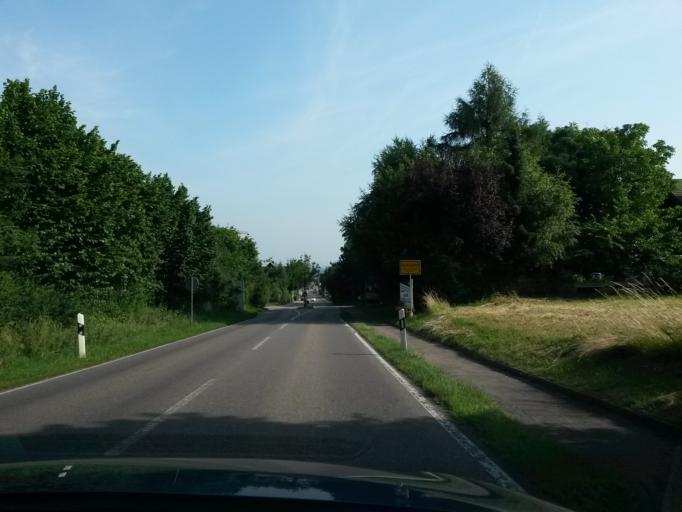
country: DE
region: Baden-Wuerttemberg
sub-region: Karlsruhe Region
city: Neuenburg
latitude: 48.8440
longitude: 8.5477
